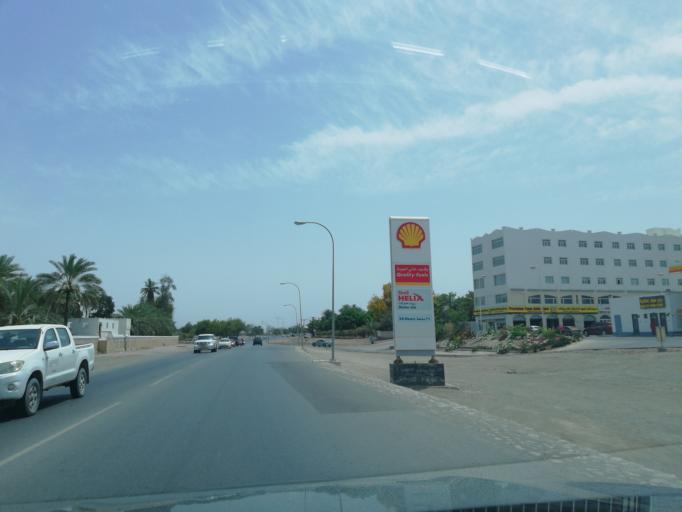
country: OM
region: Muhafazat Masqat
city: As Sib al Jadidah
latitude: 23.6787
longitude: 58.1673
